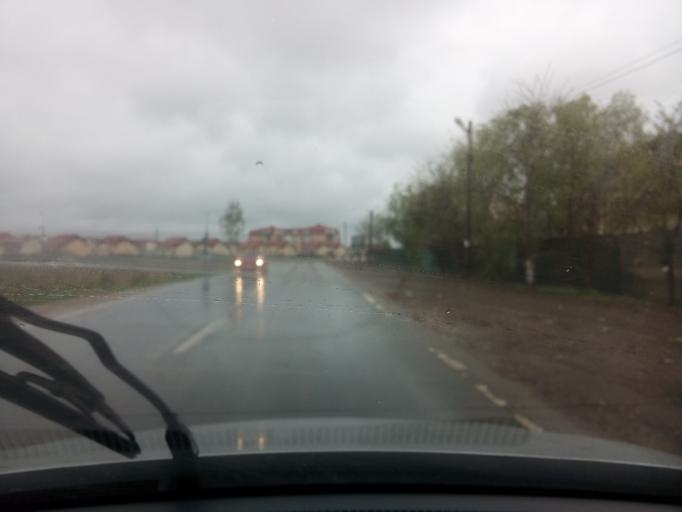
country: RO
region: Ilfov
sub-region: Voluntari City
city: Voluntari
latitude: 44.4952
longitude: 26.1464
